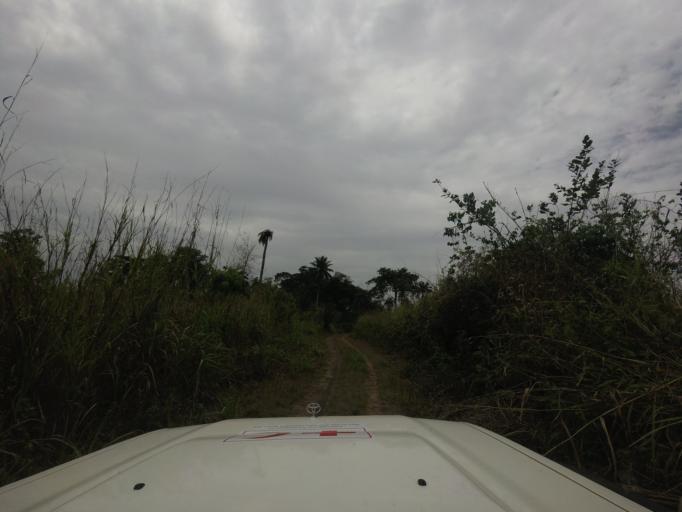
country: SL
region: Eastern Province
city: Buedu
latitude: 8.4293
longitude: -10.2661
